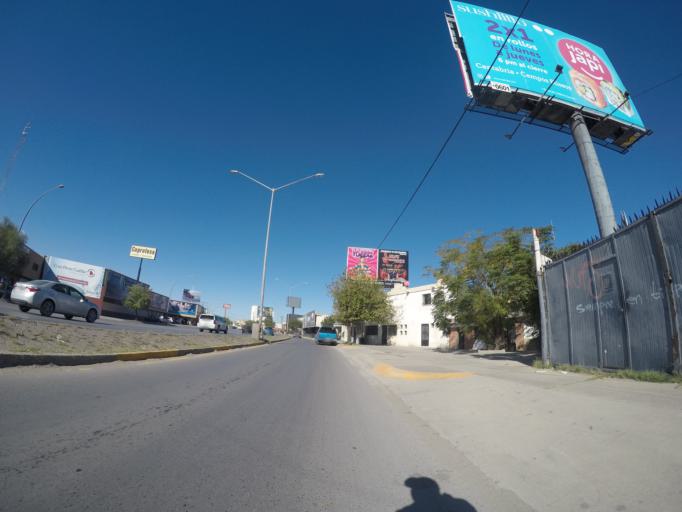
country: MX
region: Chihuahua
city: Ciudad Juarez
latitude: 31.7388
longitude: -106.4263
